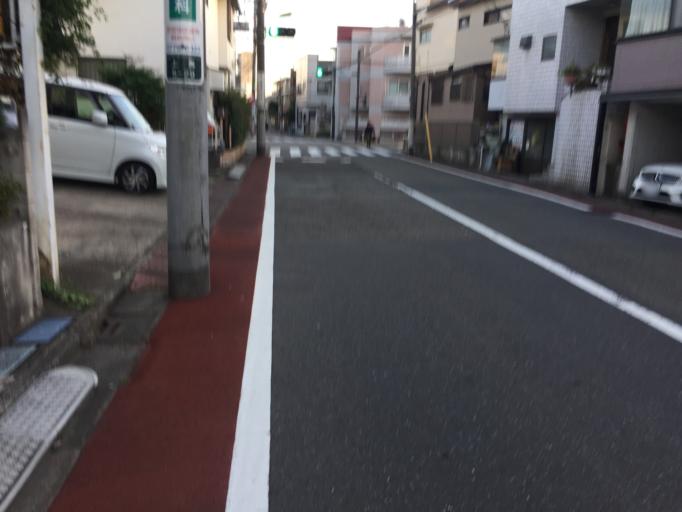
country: JP
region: Tokyo
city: Tokyo
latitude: 35.6405
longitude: 139.6575
